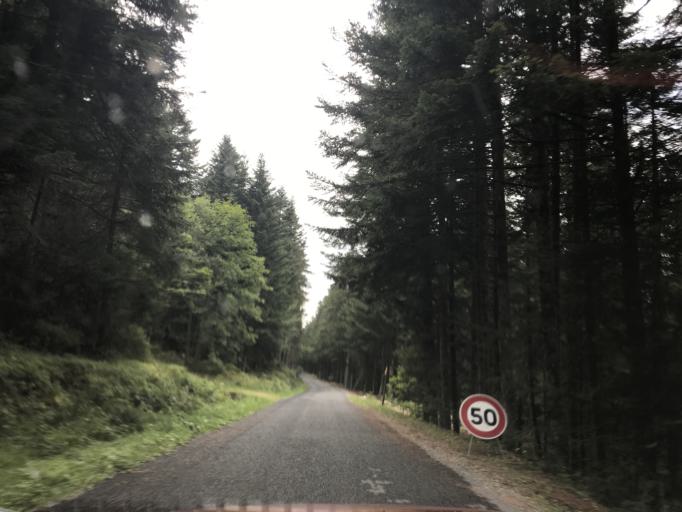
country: FR
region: Auvergne
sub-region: Departement du Puy-de-Dome
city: Job
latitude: 45.6611
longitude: 3.7718
